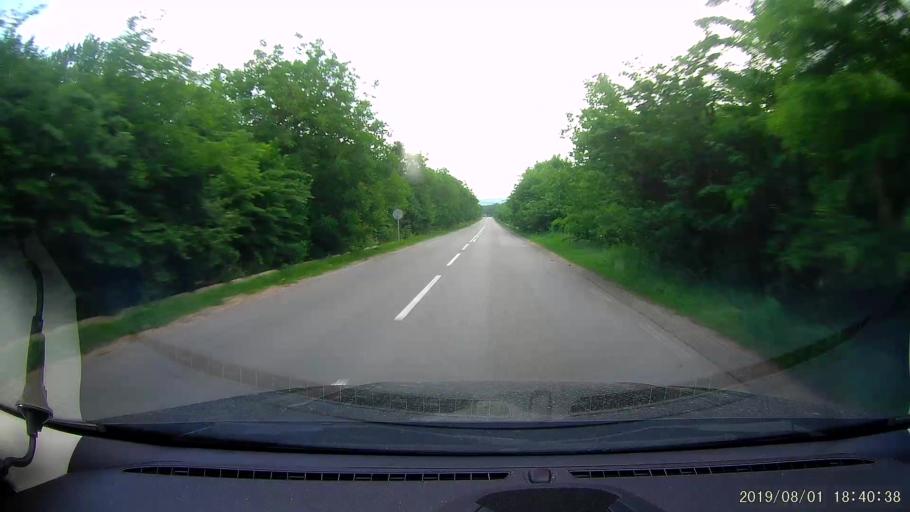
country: BG
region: Shumen
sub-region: Obshtina Khitrino
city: Gara Khitrino
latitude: 43.3625
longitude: 26.9201
